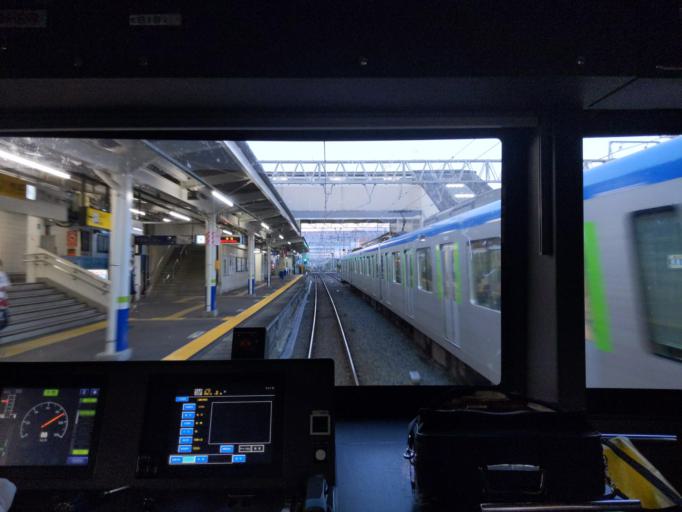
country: JP
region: Chiba
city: Shiroi
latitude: 35.7935
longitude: 139.9992
